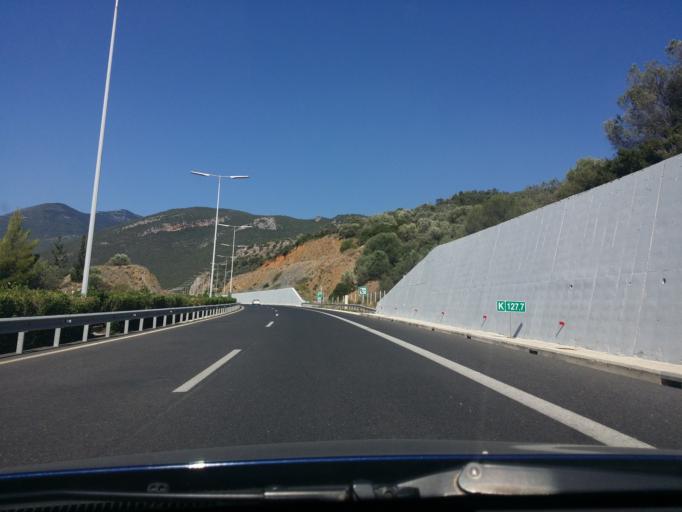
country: GR
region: Peloponnese
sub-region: Nomos Korinthias
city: Nemea
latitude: 37.7141
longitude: 22.5664
